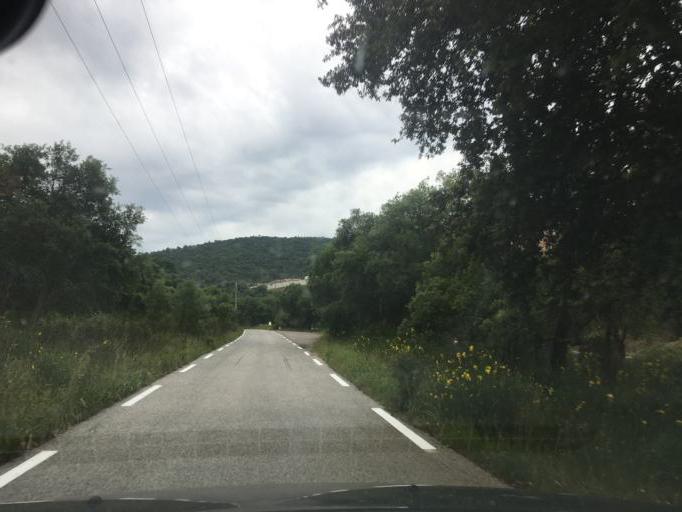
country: FR
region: Provence-Alpes-Cote d'Azur
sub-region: Departement du Var
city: Pierrefeu-du-Var
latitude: 43.2319
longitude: 6.2127
